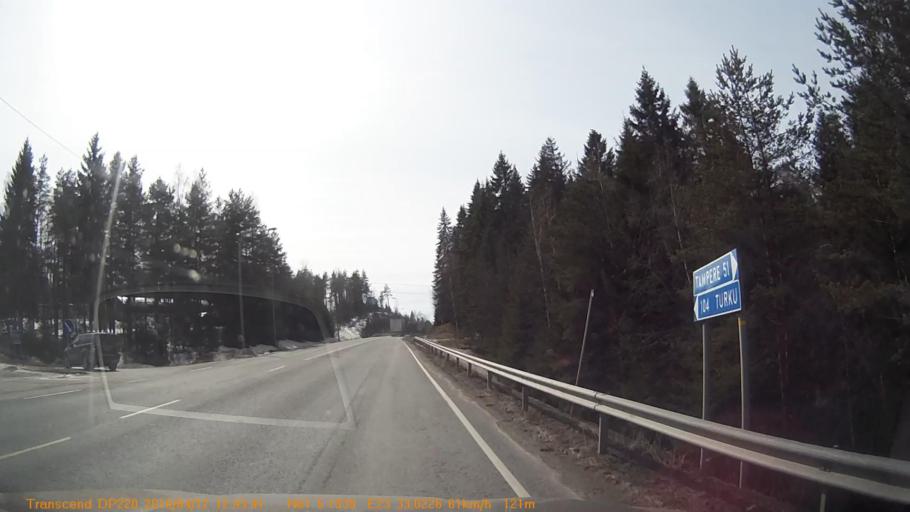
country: FI
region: Pirkanmaa
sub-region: Etelae-Pirkanmaa
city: Urjala
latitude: 61.0865
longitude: 23.5503
